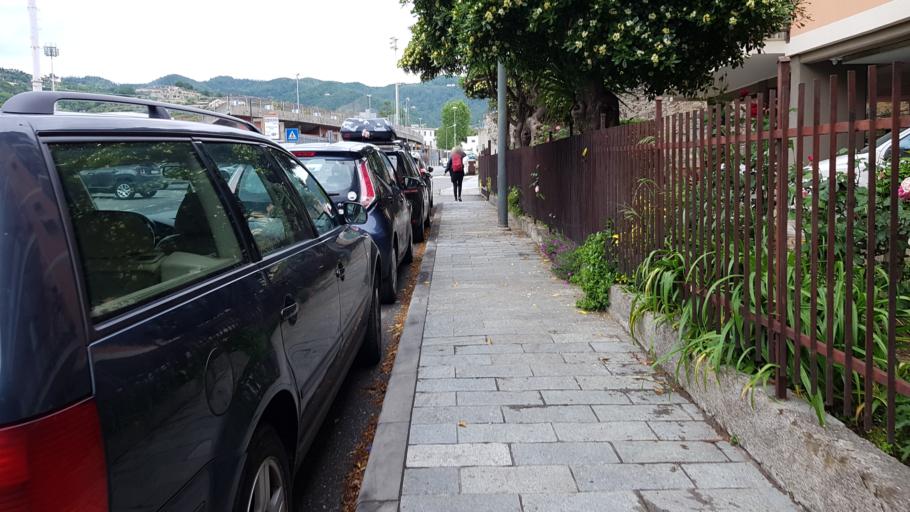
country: IT
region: Liguria
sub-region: Provincia di Savona
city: Savona
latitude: 44.2972
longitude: 8.4552
